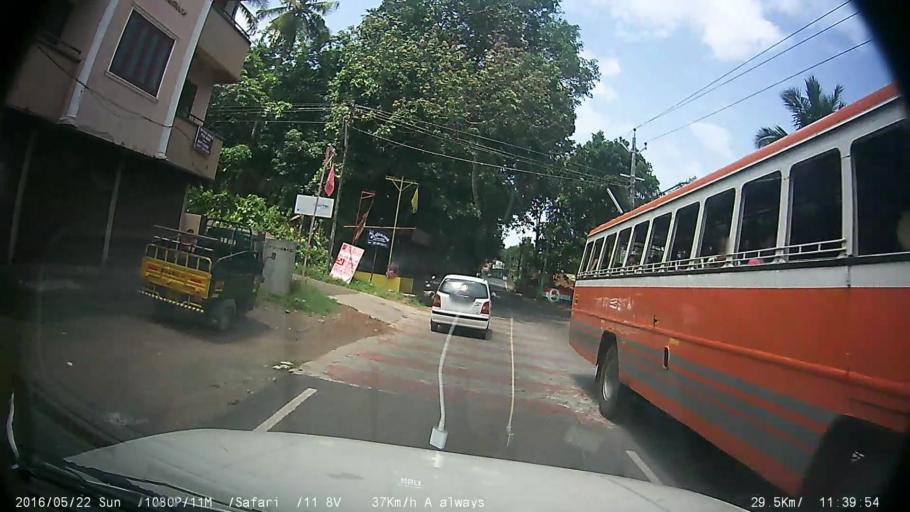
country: IN
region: Kerala
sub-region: Kottayam
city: Kottayam
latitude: 9.5581
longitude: 76.5170
